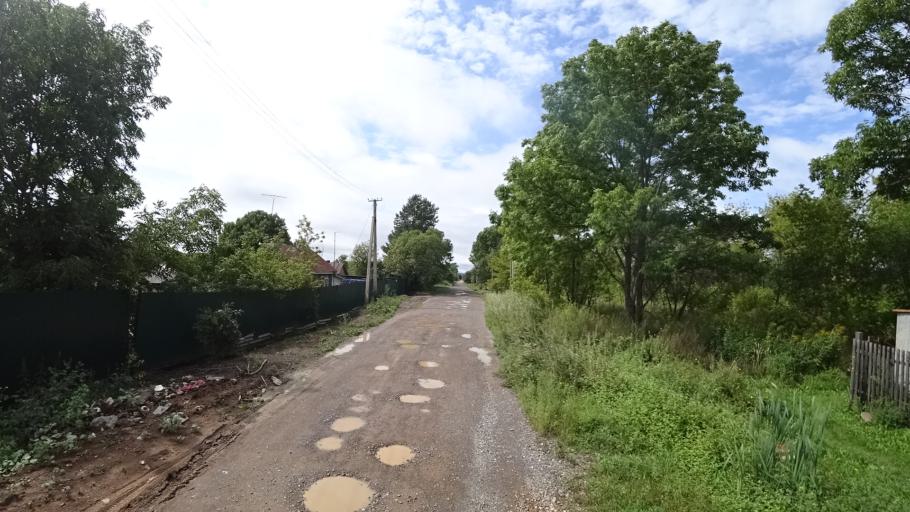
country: RU
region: Primorskiy
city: Lyalichi
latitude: 44.1387
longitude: 132.3840
